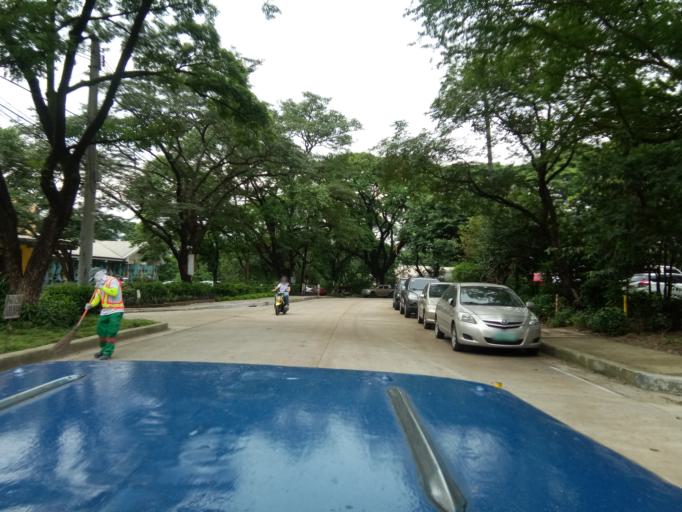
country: PH
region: Metro Manila
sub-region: Quezon City
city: Quezon City
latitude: 14.6514
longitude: 121.0655
